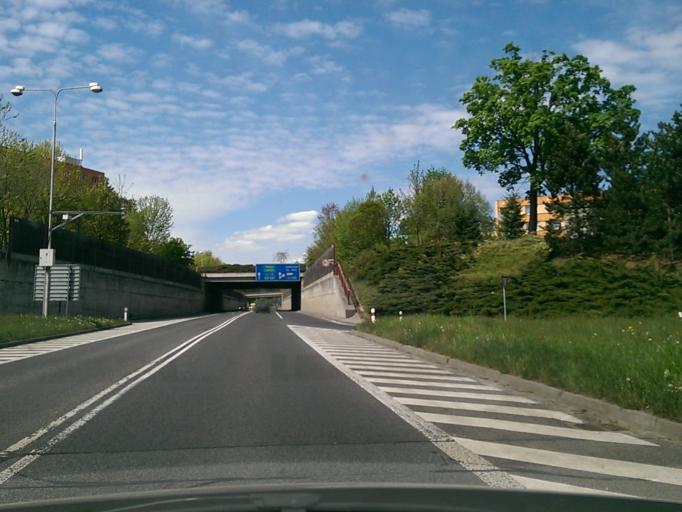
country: CZ
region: Liberecky
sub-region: Okres Semily
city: Turnov
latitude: 50.5878
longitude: 15.1446
